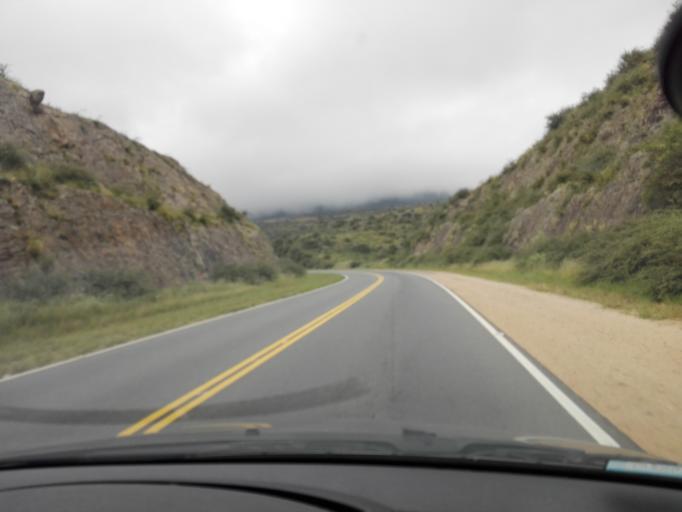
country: AR
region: Cordoba
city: Cuesta Blanca
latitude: -31.6223
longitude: -64.6708
